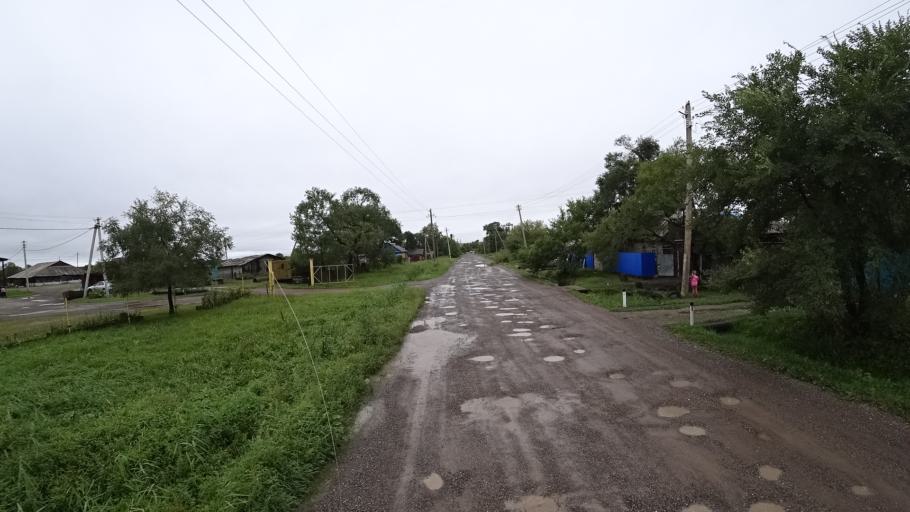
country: RU
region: Primorskiy
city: Monastyrishche
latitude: 44.1997
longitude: 132.4524
